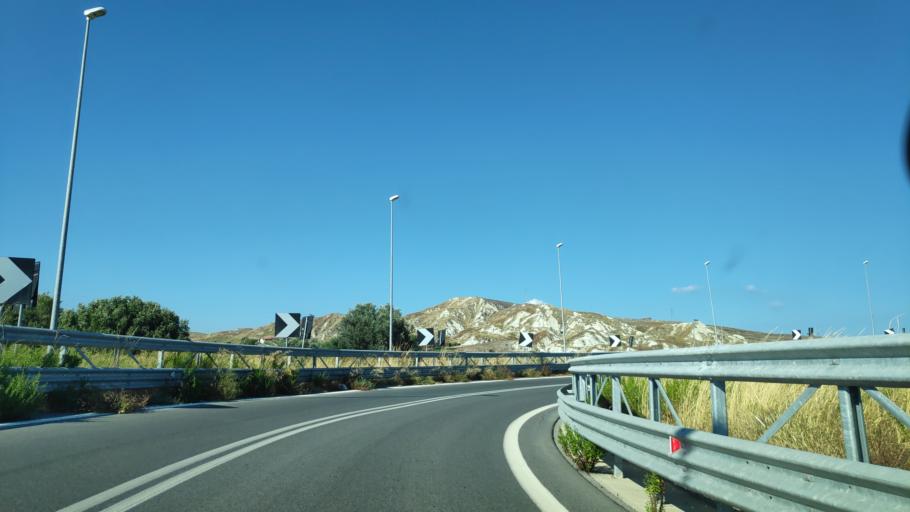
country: IT
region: Calabria
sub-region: Provincia di Reggio Calabria
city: Marina di Gioiosa Ionica
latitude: 38.3111
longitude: 16.3525
